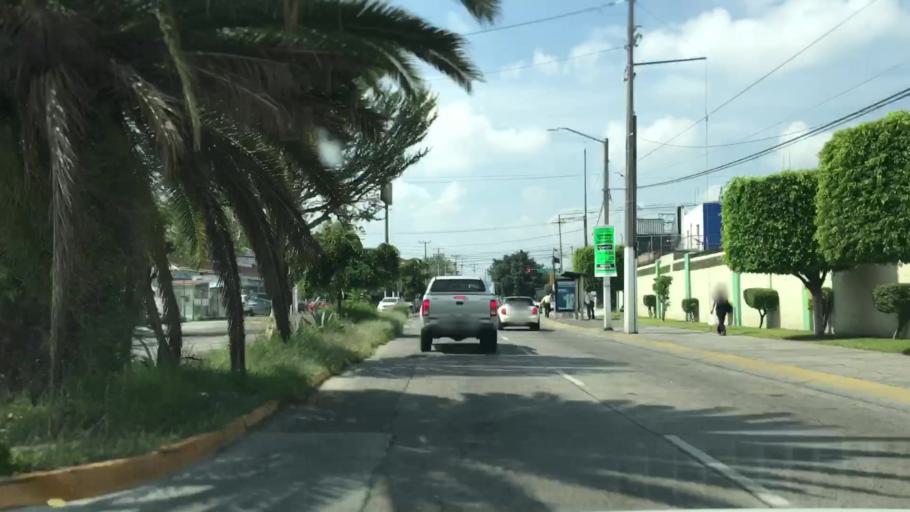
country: MX
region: Jalisco
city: Guadalajara
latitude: 20.6559
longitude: -103.4219
